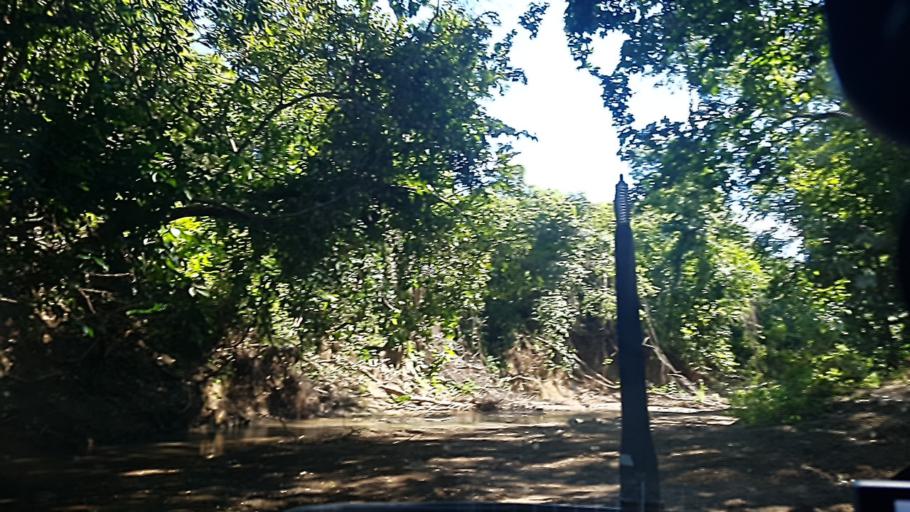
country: NI
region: Rivas
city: Tola
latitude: 11.5432
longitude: -86.0982
